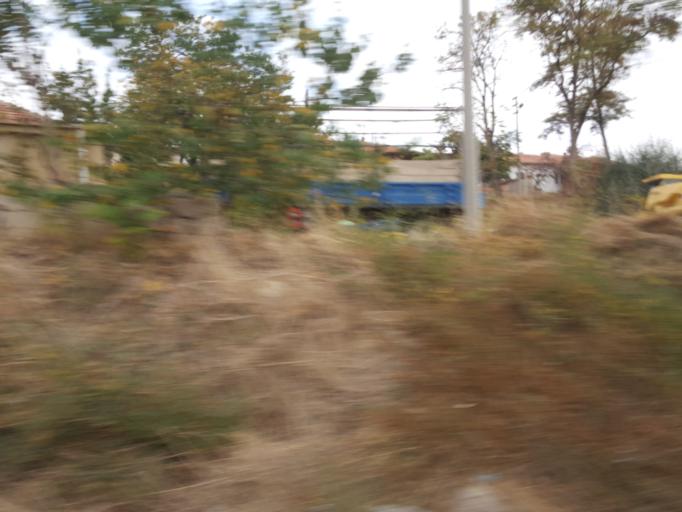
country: TR
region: Kirikkale
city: Keskin
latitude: 39.6736
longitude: 33.6050
